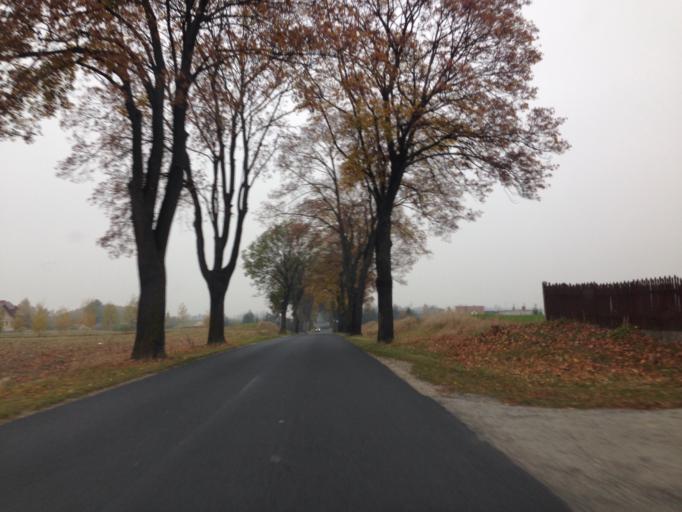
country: PL
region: Kujawsko-Pomorskie
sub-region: Powiat brodnicki
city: Brodnica
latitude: 53.3179
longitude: 19.3837
